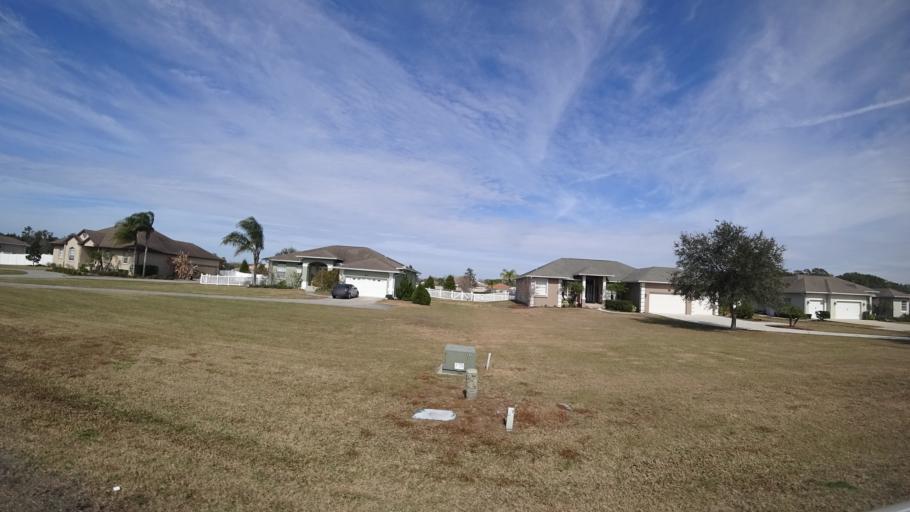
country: US
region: Florida
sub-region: Manatee County
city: Ellenton
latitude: 27.5135
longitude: -82.3736
